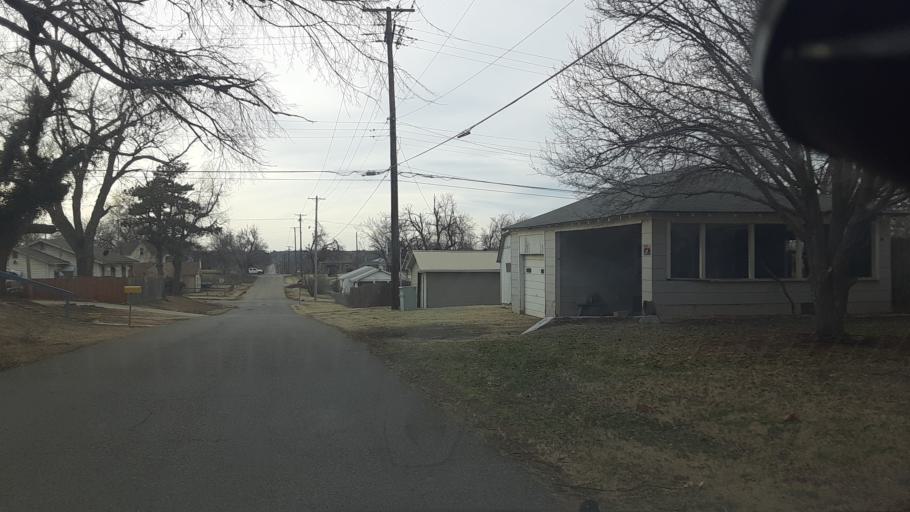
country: US
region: Oklahoma
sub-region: Logan County
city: Guthrie
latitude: 35.8853
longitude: -97.4218
